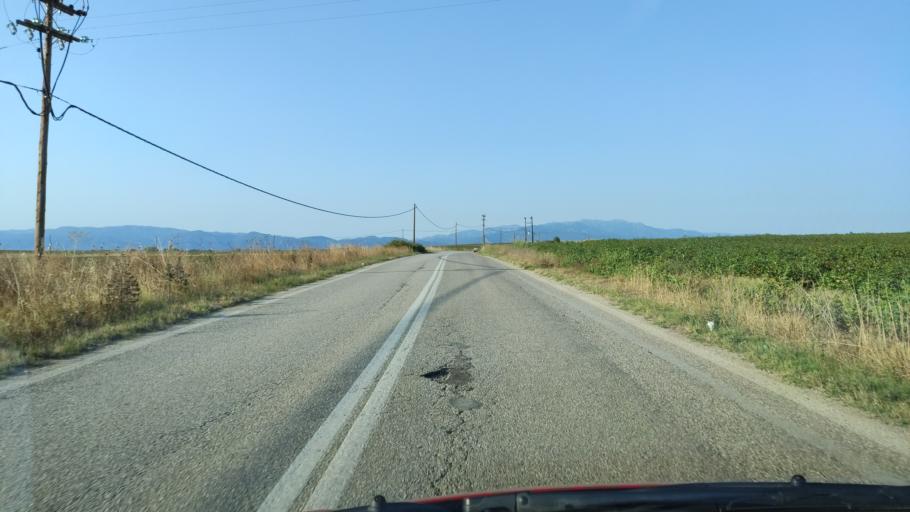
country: GR
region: East Macedonia and Thrace
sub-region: Nomos Rodopis
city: Iasmos
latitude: 40.9848
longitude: 25.1595
